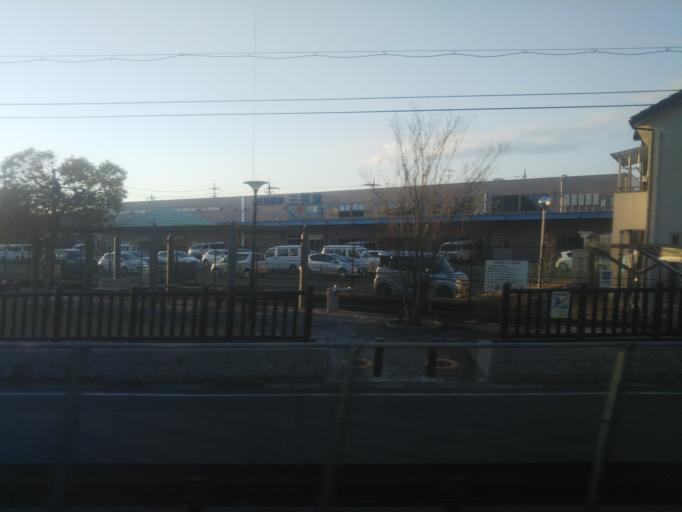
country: JP
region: Shiga Prefecture
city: Kusatsu
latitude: 35.0273
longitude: 136.0045
